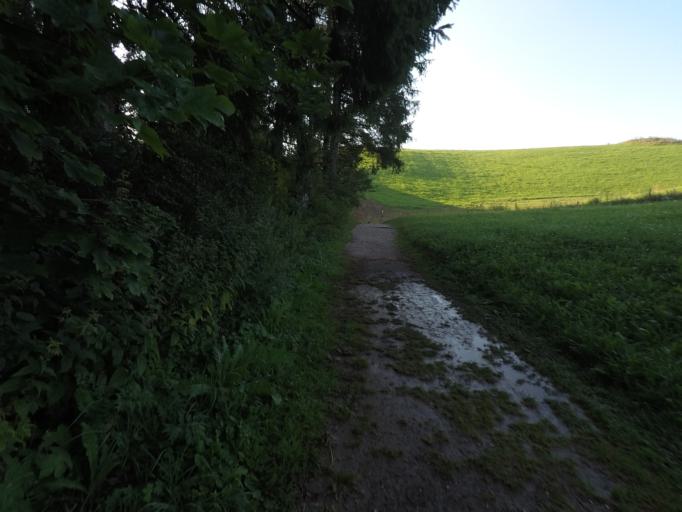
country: IT
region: Veneto
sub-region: Provincia di Vicenza
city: Asiago
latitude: 45.8622
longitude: 11.5273
